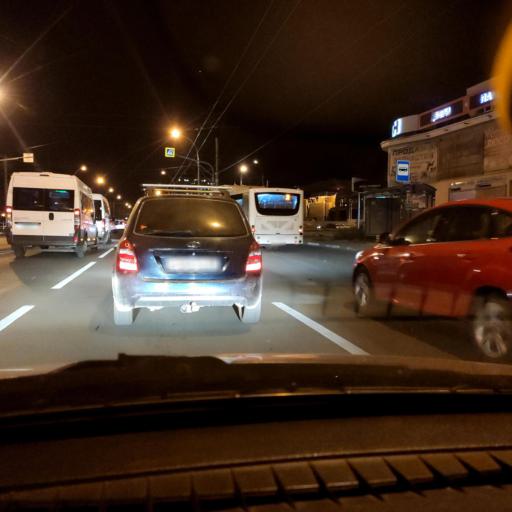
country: RU
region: Samara
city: Tol'yatti
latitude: 53.5072
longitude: 49.2693
